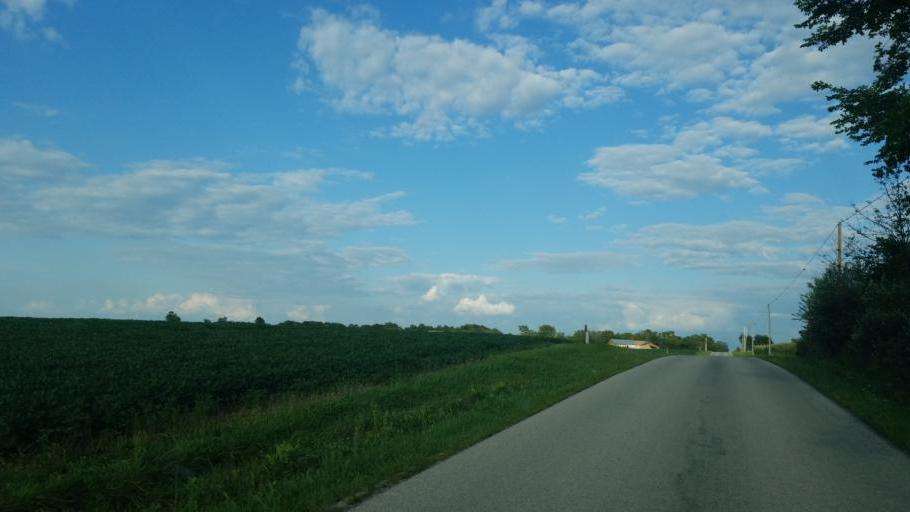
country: US
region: Ohio
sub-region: Sandusky County
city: Green Springs
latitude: 41.1101
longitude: -83.0195
